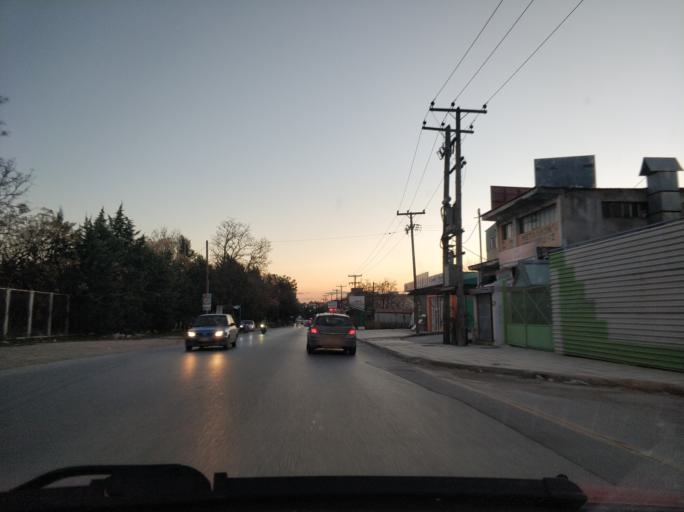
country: GR
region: Central Macedonia
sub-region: Nomos Thessalonikis
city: Efkarpia
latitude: 40.6791
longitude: 22.9465
